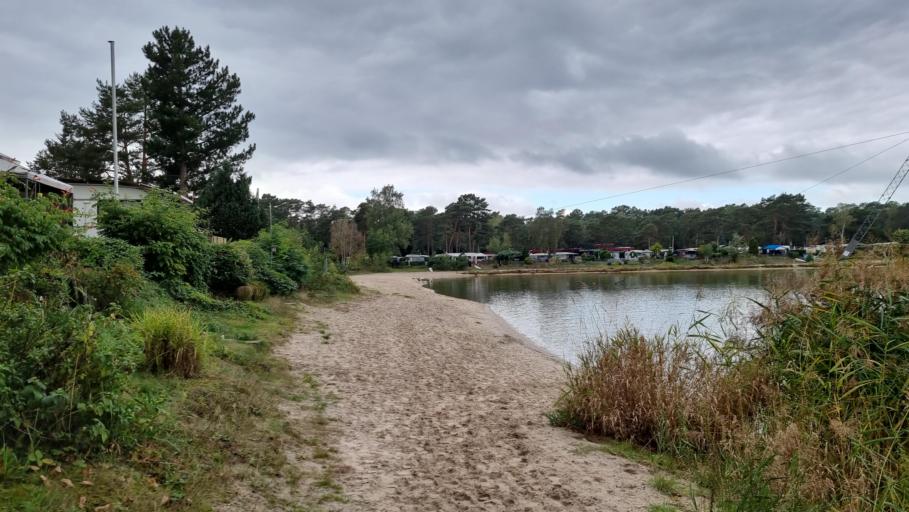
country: DE
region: Lower Saxony
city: Garbsen
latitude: 52.4189
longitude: 9.5492
